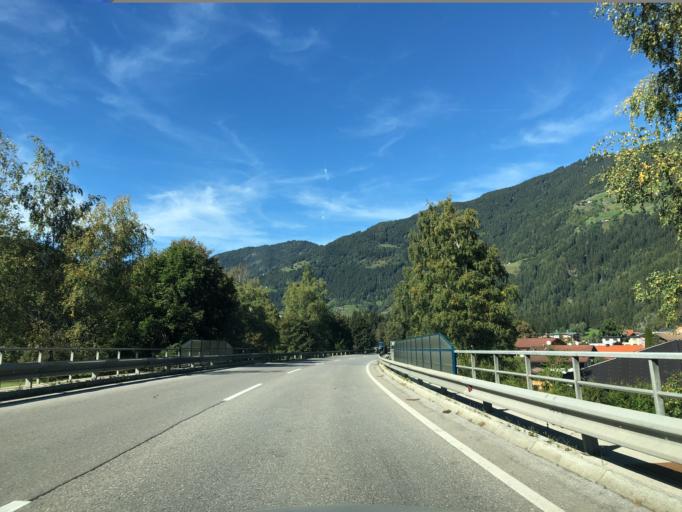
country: AT
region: Tyrol
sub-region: Politischer Bezirk Imst
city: Oetz
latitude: 47.1879
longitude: 10.9065
